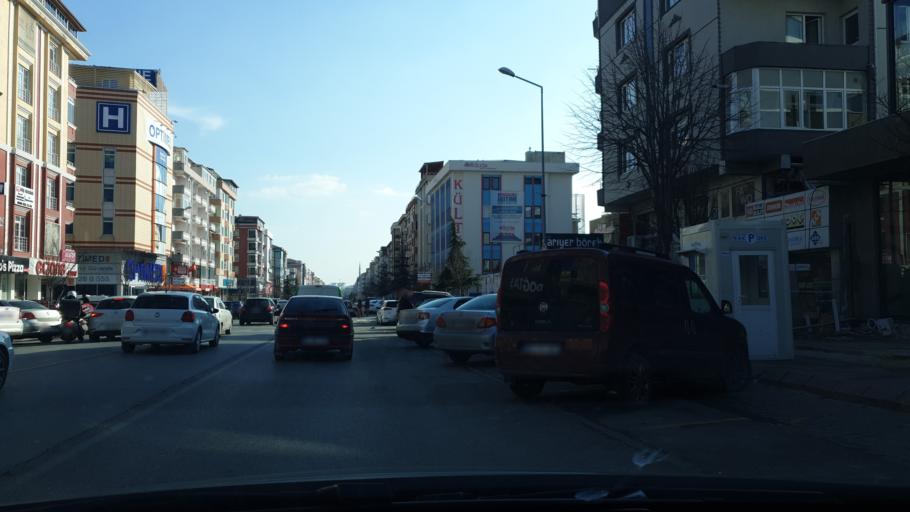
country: TR
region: Tekirdag
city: Cerkezkoey
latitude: 41.2953
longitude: 27.9975
